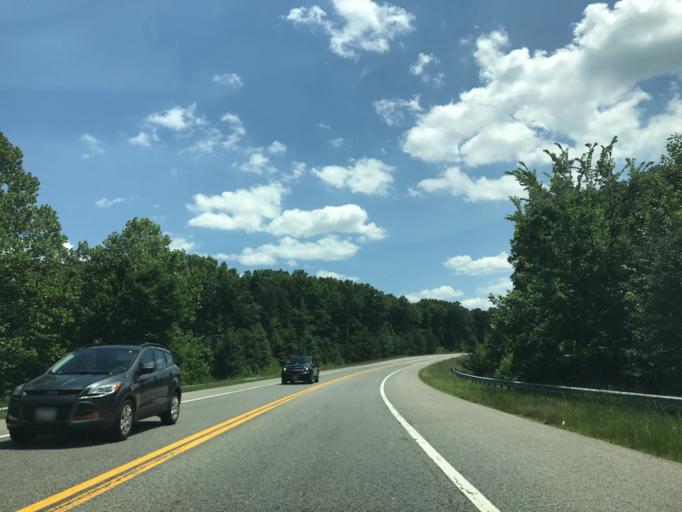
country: US
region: Maryland
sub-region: Prince George's County
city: Glenn Dale
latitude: 39.0262
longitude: -76.7717
